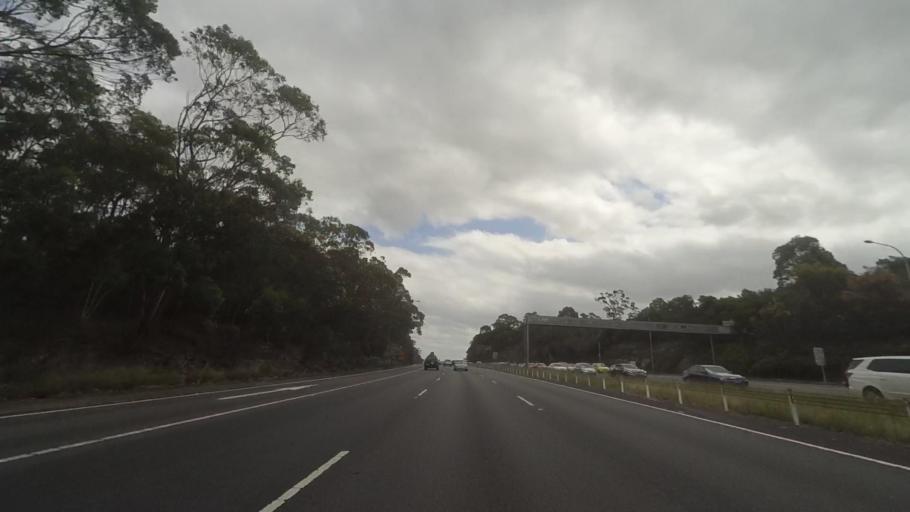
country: AU
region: New South Wales
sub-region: Gosford Shire
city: Point Clare
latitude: -33.4551
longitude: 151.2059
